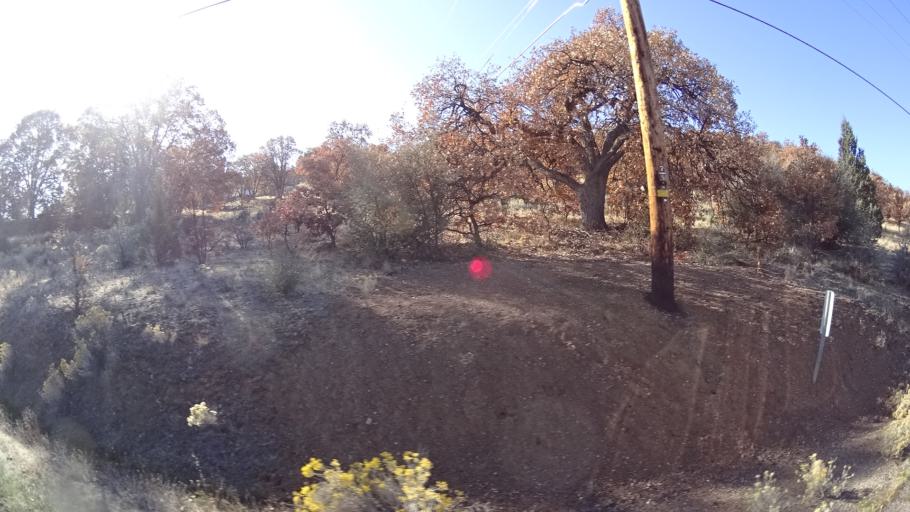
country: US
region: California
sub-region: Siskiyou County
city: Yreka
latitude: 41.7388
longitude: -122.6086
